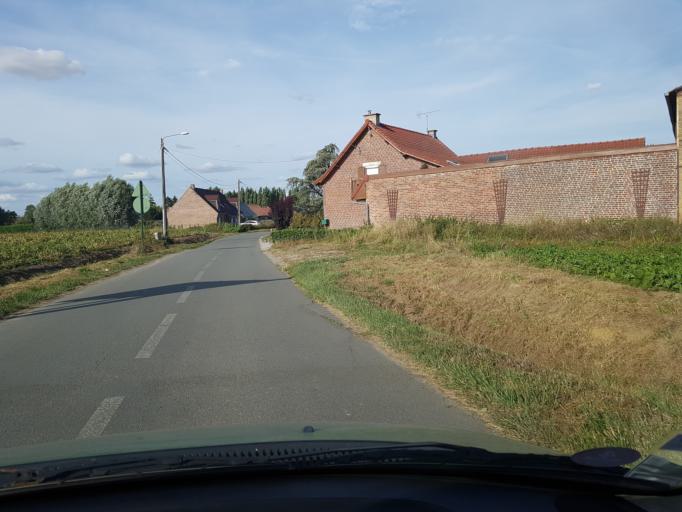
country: FR
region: Nord-Pas-de-Calais
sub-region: Departement du Pas-de-Calais
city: Locon
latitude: 50.5711
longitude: 2.6498
